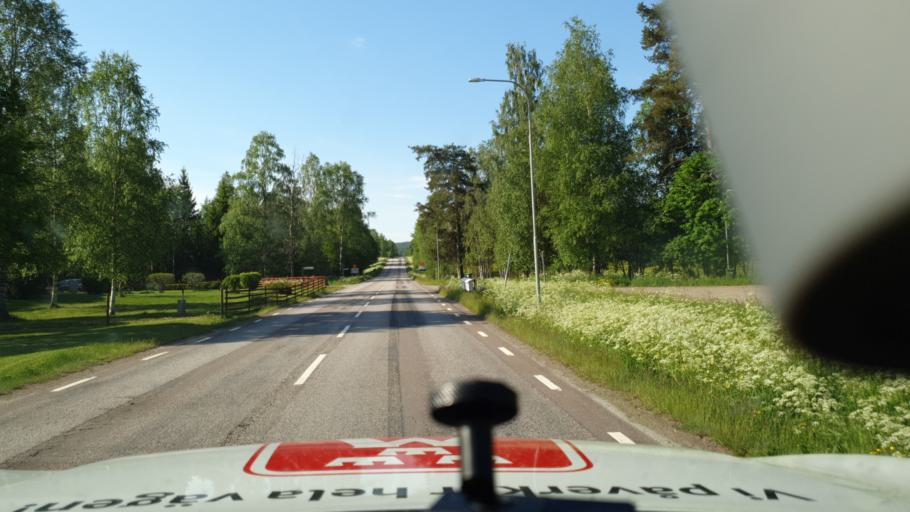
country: SE
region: Vaermland
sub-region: Torsby Kommun
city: Torsby
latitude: 59.9419
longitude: 12.9025
